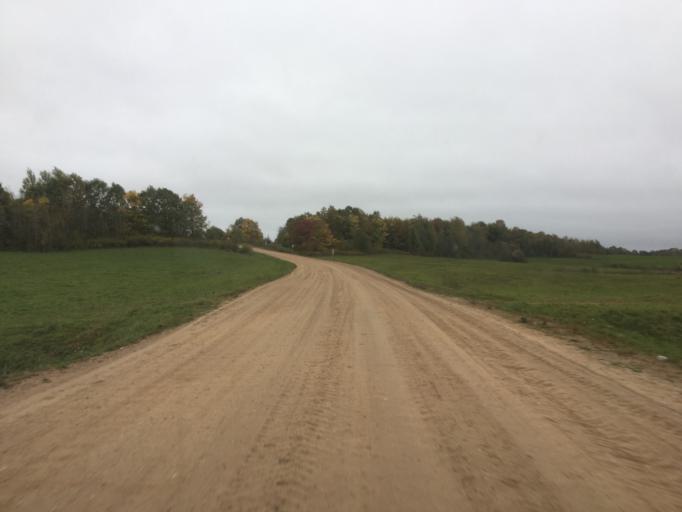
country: BY
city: Novolukoml'
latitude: 54.7169
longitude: 29.1389
